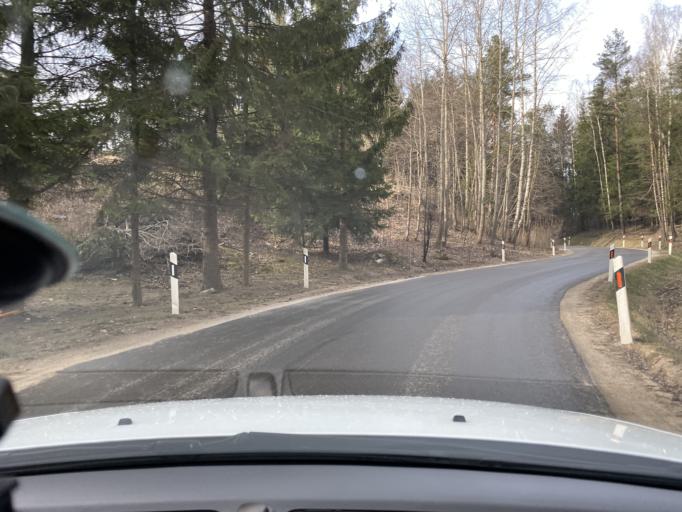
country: LT
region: Vilnius County
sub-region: Vilnius
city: Fabijoniskes
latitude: 54.7593
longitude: 25.2547
